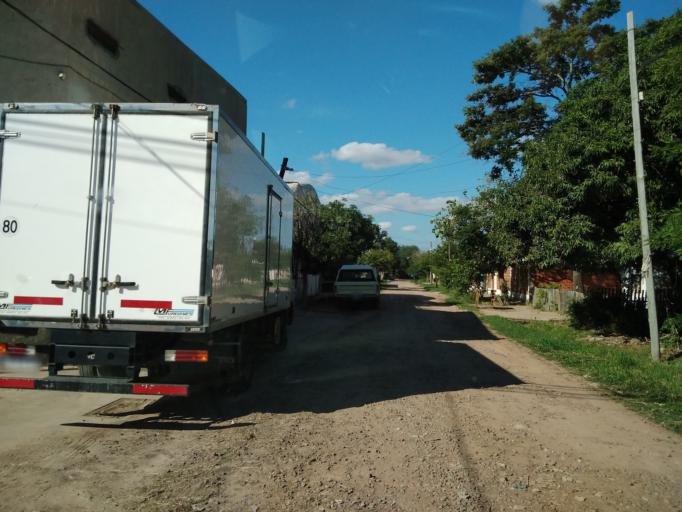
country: AR
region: Corrientes
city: Corrientes
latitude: -27.4629
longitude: -58.7785
